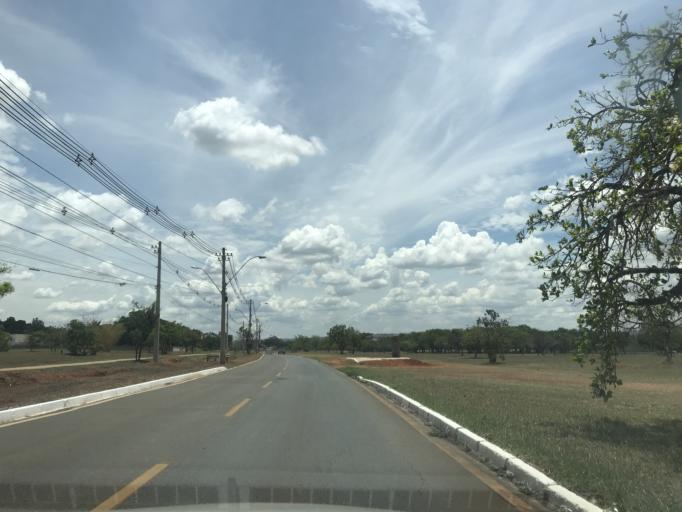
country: BR
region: Federal District
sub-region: Brasilia
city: Brasilia
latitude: -15.8661
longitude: -47.9383
